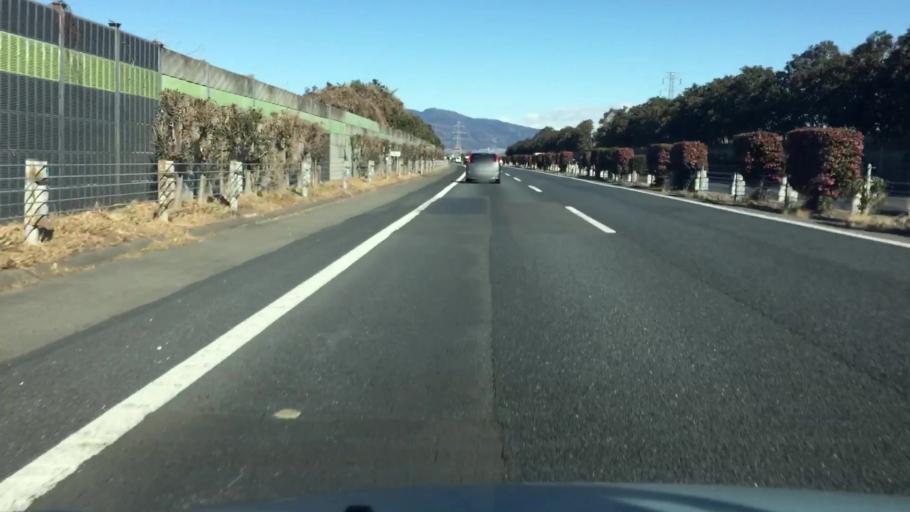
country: JP
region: Gunma
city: Kanekomachi
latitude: 36.4455
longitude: 139.0148
